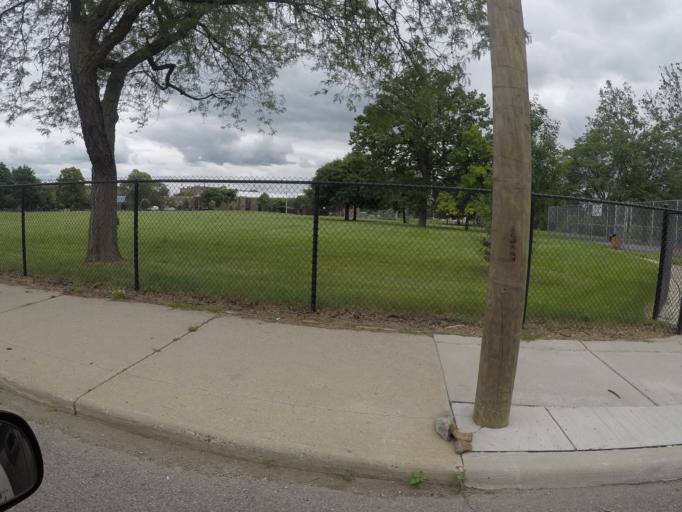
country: US
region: Michigan
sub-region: Wayne County
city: Detroit
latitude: 42.3594
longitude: -83.0040
